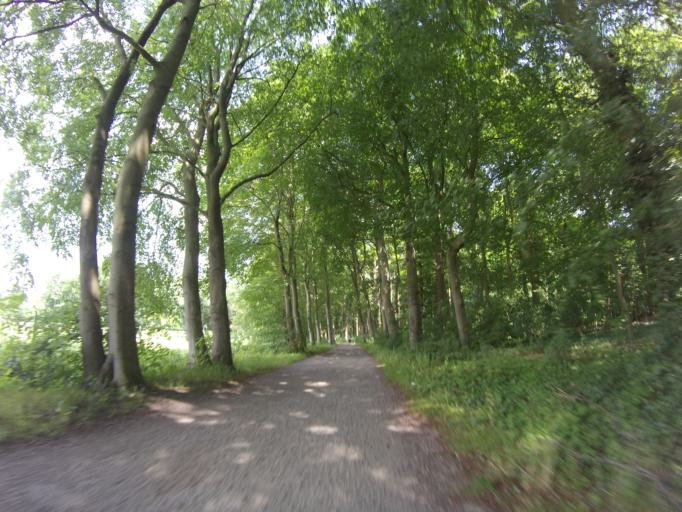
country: NL
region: Utrecht
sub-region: Gemeente De Bilt
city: De Bilt
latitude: 52.1278
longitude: 5.1566
